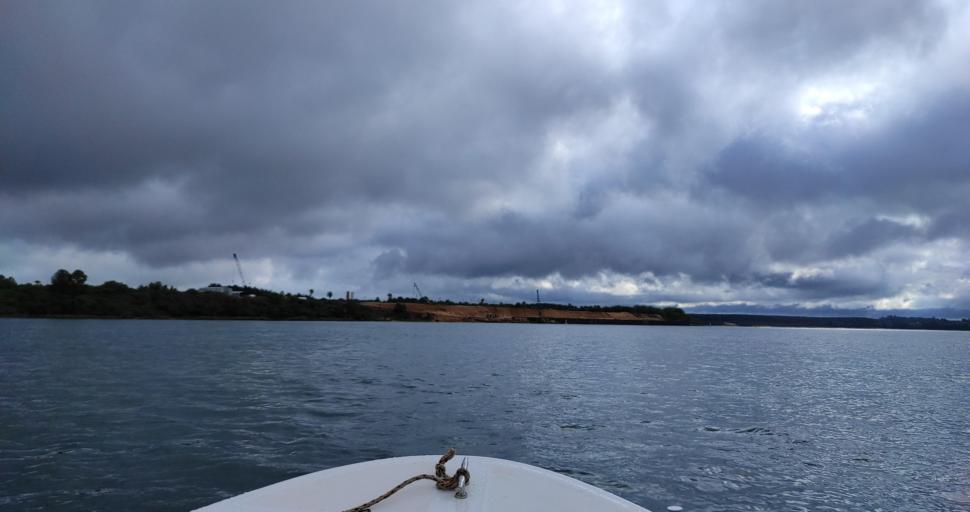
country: AR
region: Corrientes
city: Ituzaingo
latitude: -27.6064
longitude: -56.8292
